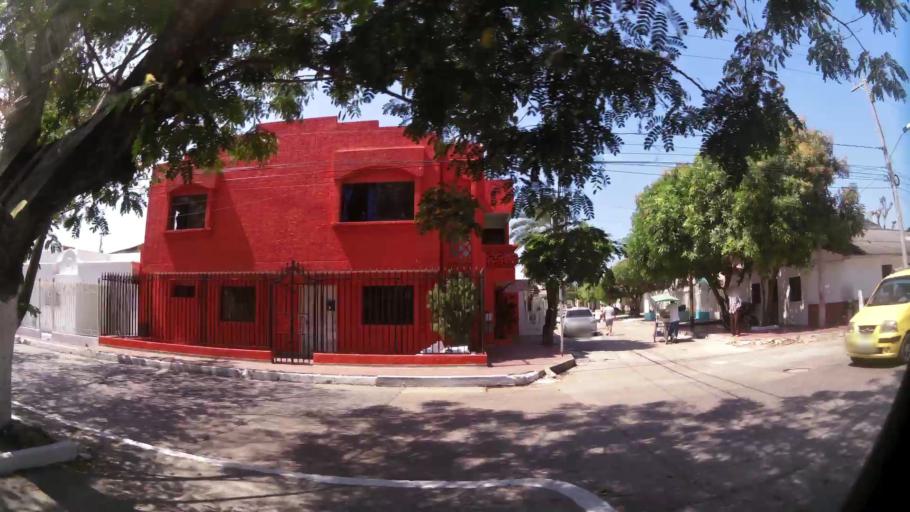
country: CO
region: Atlantico
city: Barranquilla
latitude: 10.9710
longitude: -74.8058
